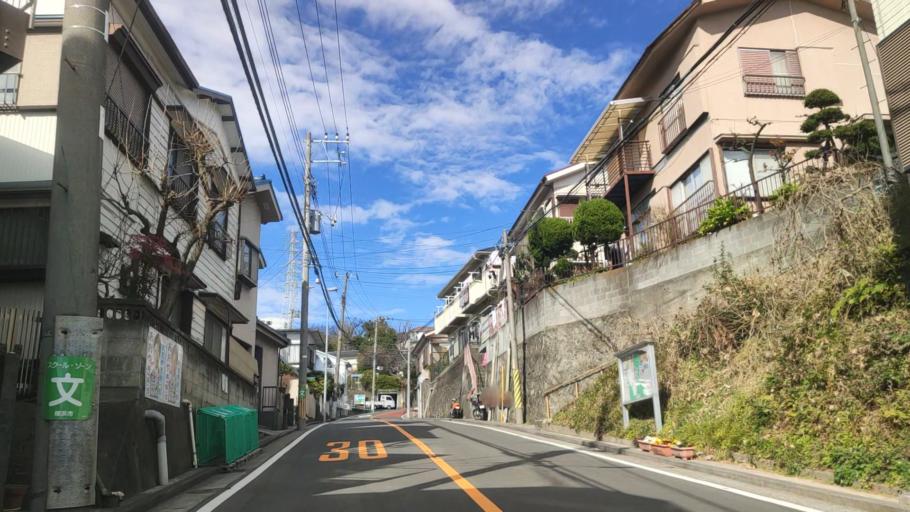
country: JP
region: Kanagawa
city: Yokohama
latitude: 35.4666
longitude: 139.5852
